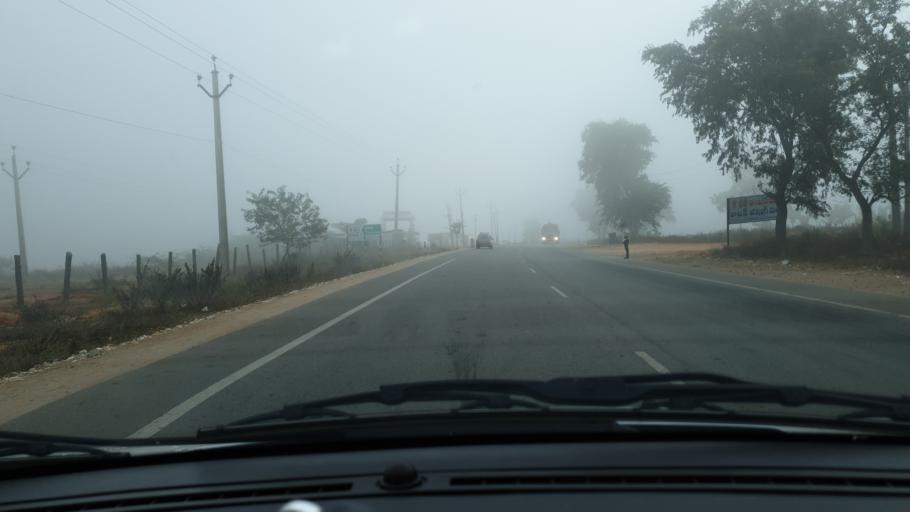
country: IN
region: Telangana
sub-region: Mahbubnagar
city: Nagar Karnul
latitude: 16.6648
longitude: 78.5567
